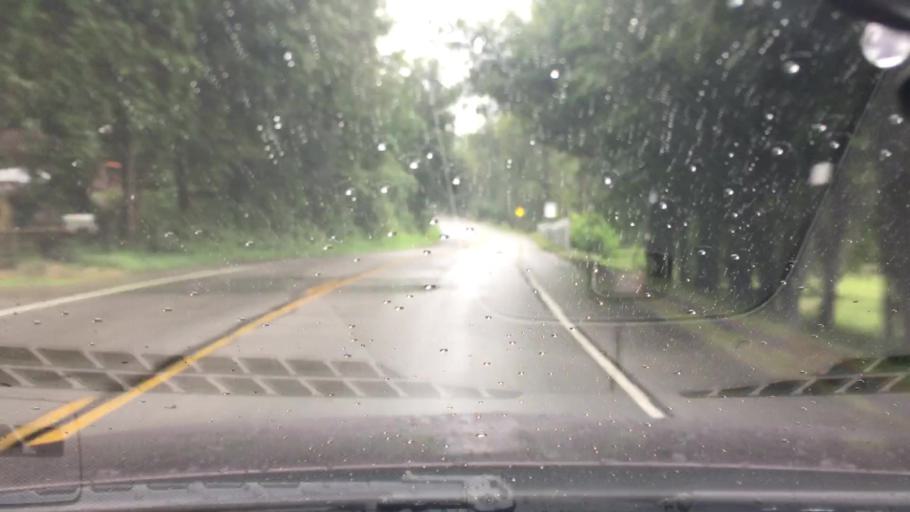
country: US
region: New York
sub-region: Dutchess County
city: Brinckerhoff
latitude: 41.5534
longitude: -73.8258
